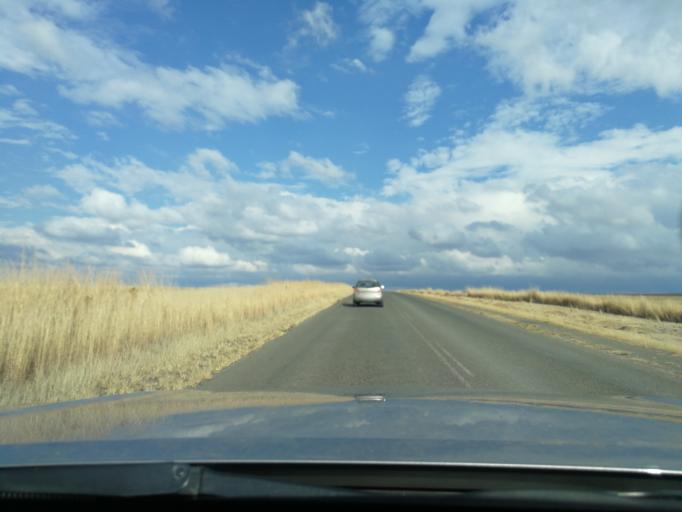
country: ZA
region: Orange Free State
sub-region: Fezile Dabi District Municipality
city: Frankfort
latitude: -27.4506
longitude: 28.5174
